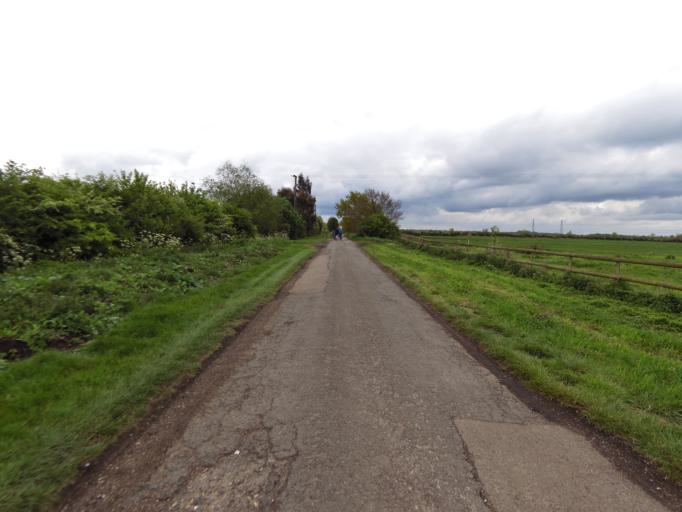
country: GB
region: England
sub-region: Cambridgeshire
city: Bottisham
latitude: 52.2753
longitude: 0.2685
